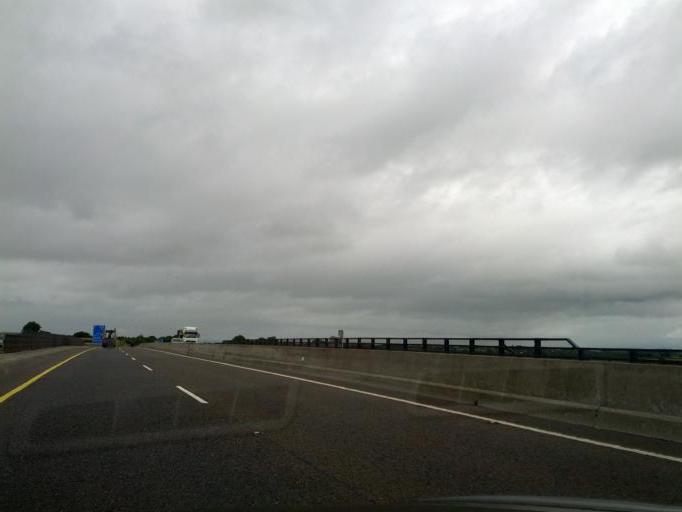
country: IE
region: Munster
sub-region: An Clar
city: Ennis
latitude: 52.8109
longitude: -8.9331
